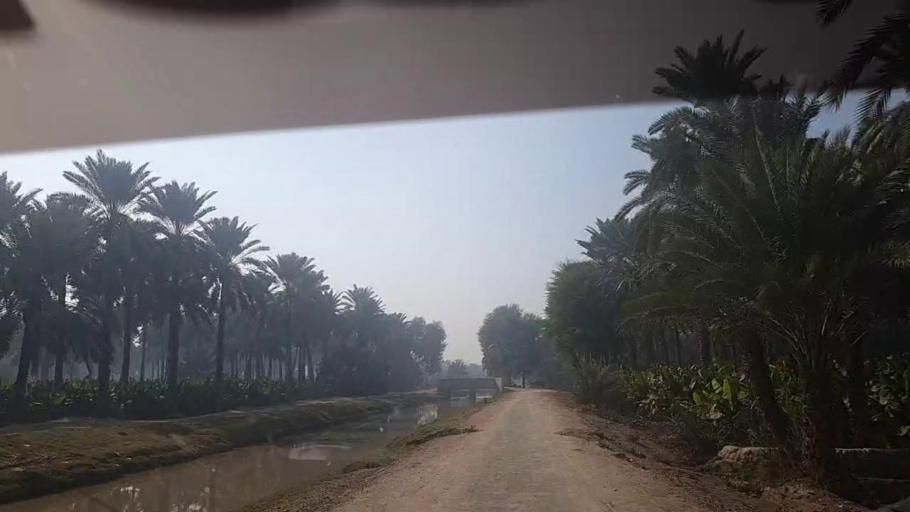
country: PK
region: Sindh
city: Khairpur
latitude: 27.4625
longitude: 68.7086
